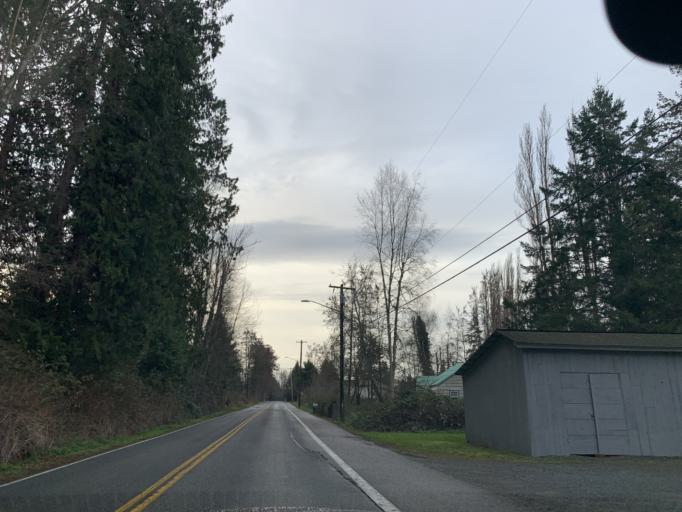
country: US
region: Washington
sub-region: Snohomish County
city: Marysville
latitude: 48.0845
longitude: -122.1565
